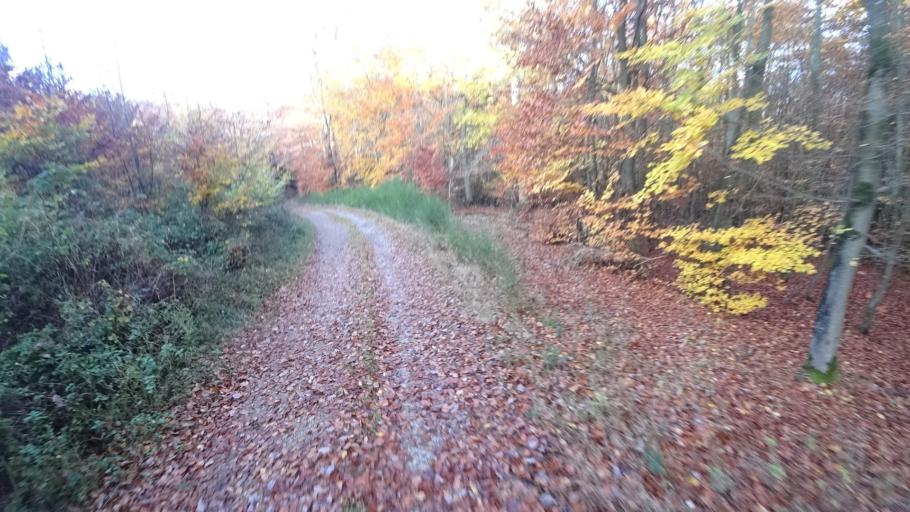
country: DE
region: Rheinland-Pfalz
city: Badenhard
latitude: 50.1220
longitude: 7.6544
